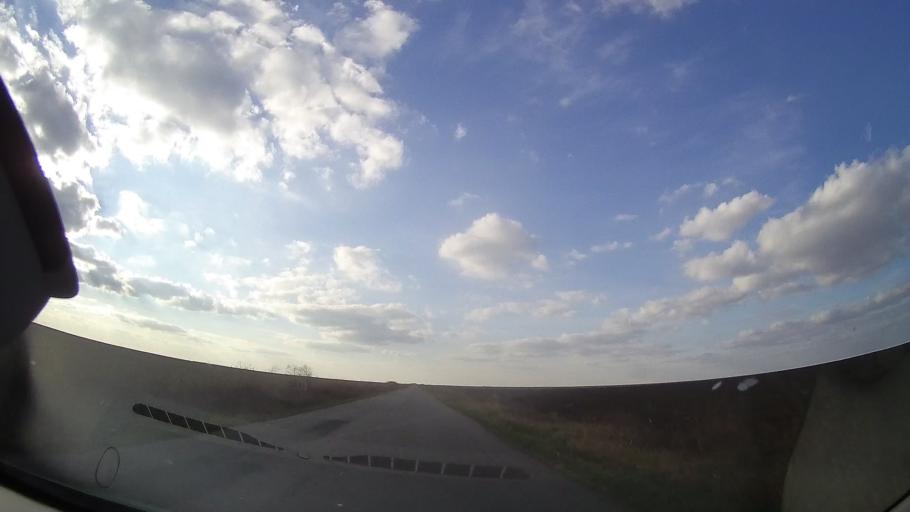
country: RO
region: Constanta
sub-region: Comuna Negru Voda
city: Negru Voda
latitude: 43.8227
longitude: 28.1530
